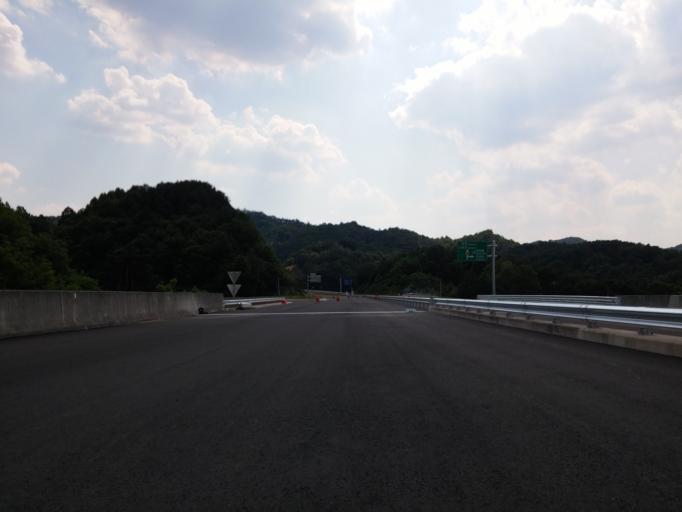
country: KR
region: Daejeon
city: Sintansin
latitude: 36.5027
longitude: 127.4746
